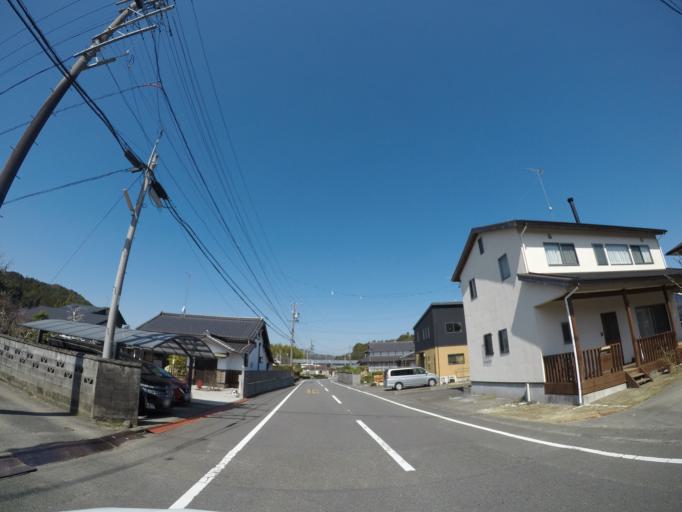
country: JP
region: Shizuoka
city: Kanaya
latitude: 34.7741
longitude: 138.1104
